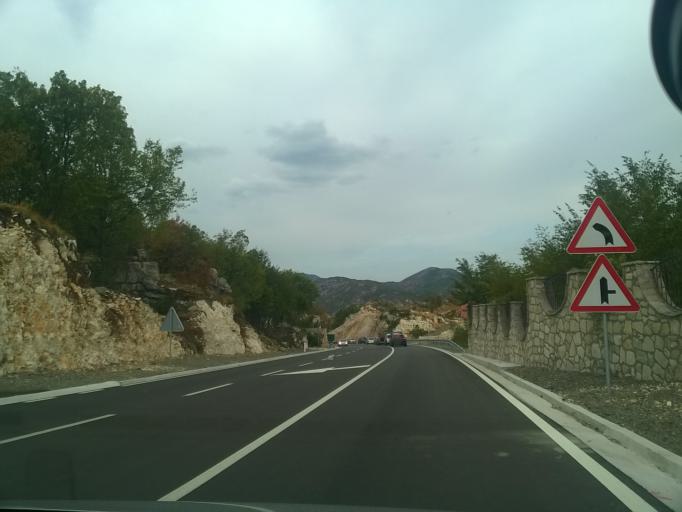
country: ME
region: Cetinje
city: Cetinje
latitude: 42.3875
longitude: 18.9388
